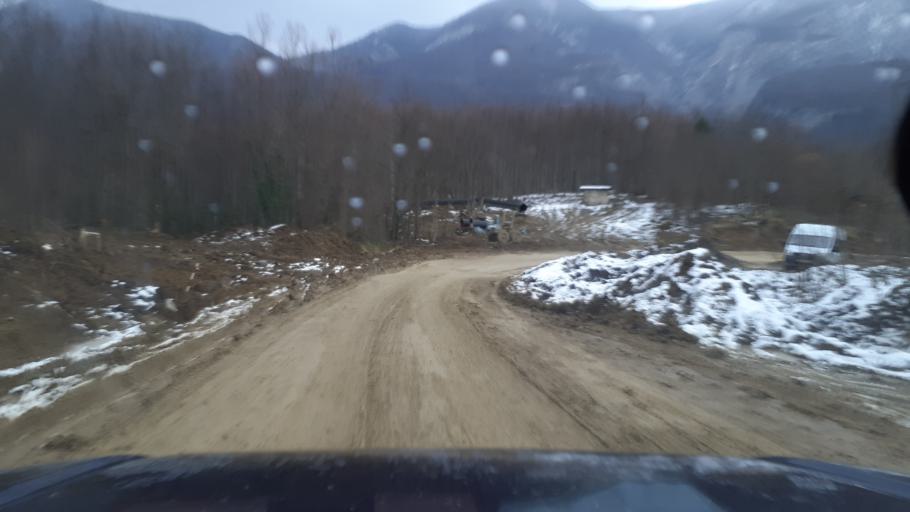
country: RU
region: Krasnodarskiy
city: Neftegorsk
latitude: 44.1641
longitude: 39.8202
